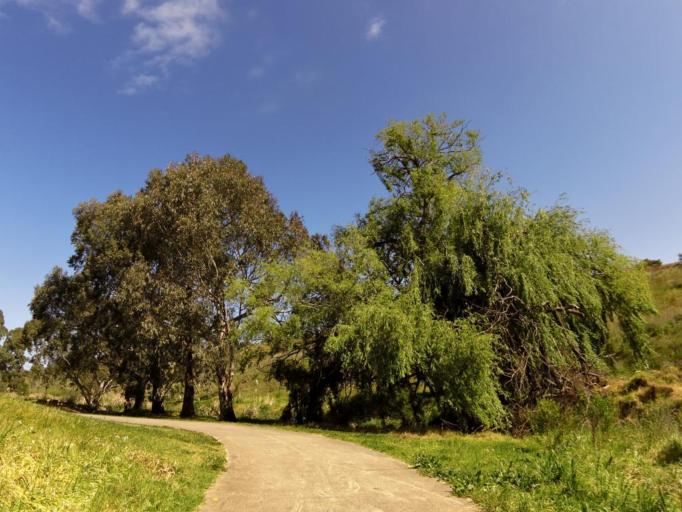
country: AU
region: Victoria
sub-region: Moonee Valley
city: Essendon West
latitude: -37.7573
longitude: 144.8877
